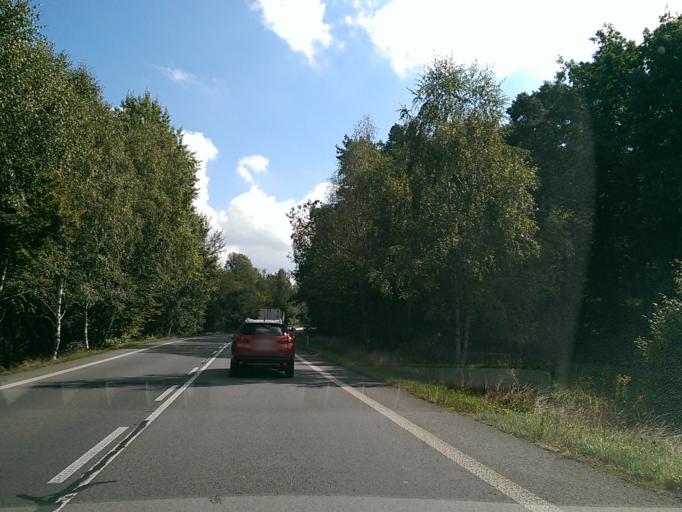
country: CZ
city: Doksy
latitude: 50.5865
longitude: 14.6244
